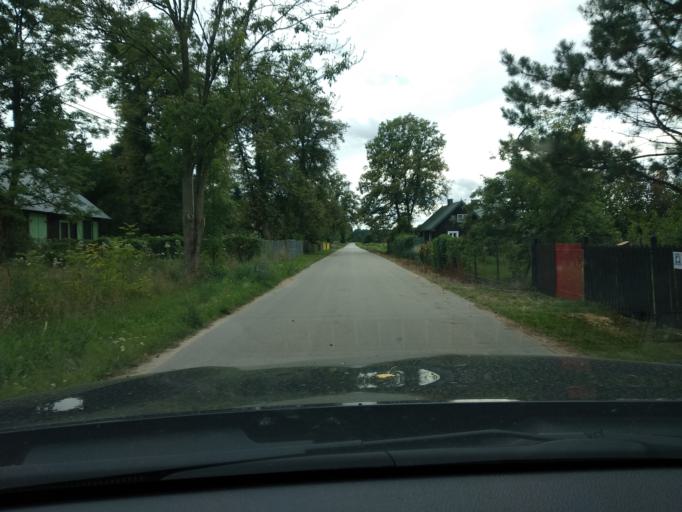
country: PL
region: Masovian Voivodeship
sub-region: Powiat pultuski
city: Obryte
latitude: 52.7382
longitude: 21.1735
